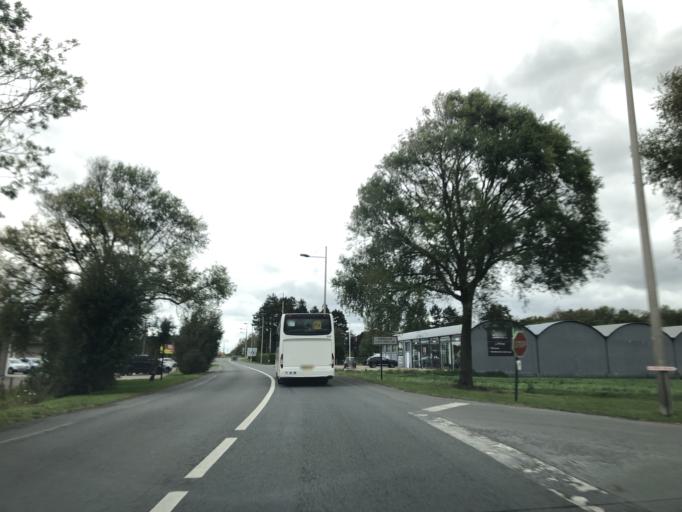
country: FR
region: Nord-Pas-de-Calais
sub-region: Departement du Pas-de-Calais
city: Saint-Josse
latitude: 50.4608
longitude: 1.6501
